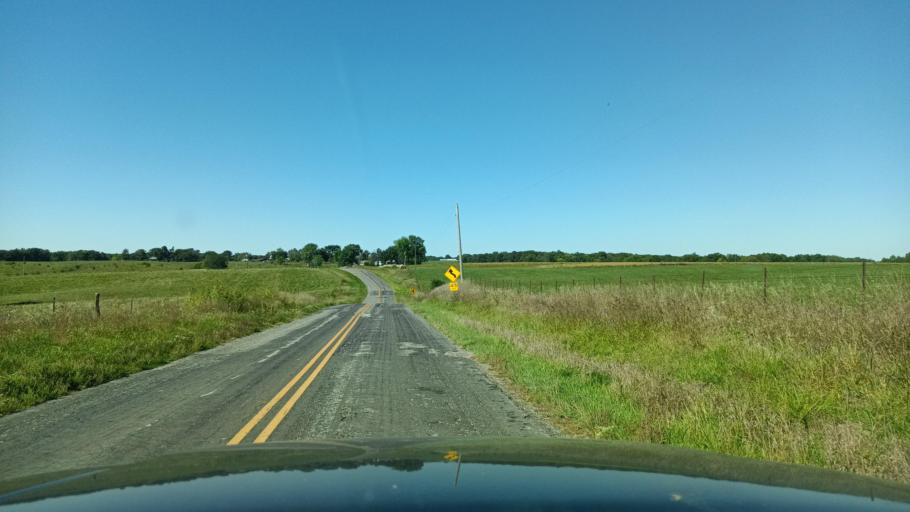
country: US
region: Missouri
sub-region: Scotland County
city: Memphis
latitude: 40.3541
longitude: -92.2906
